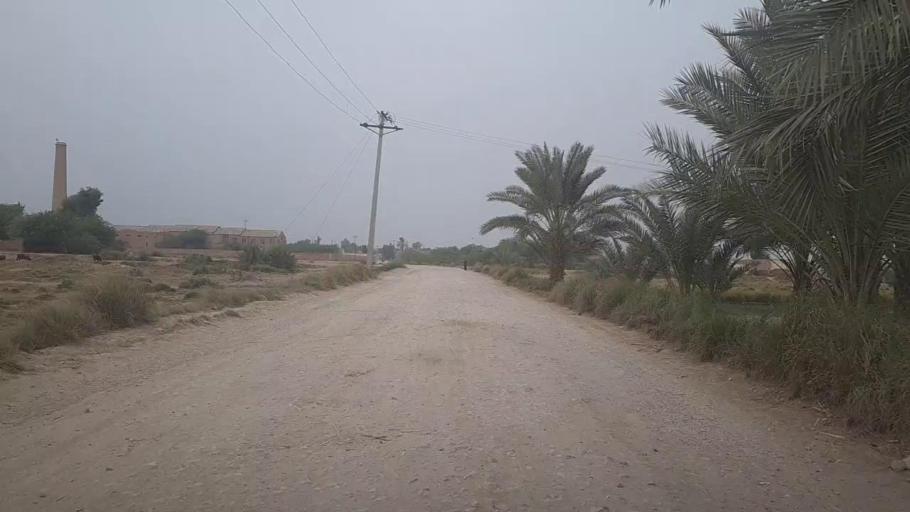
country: PK
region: Sindh
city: Gambat
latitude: 27.3355
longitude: 68.5493
